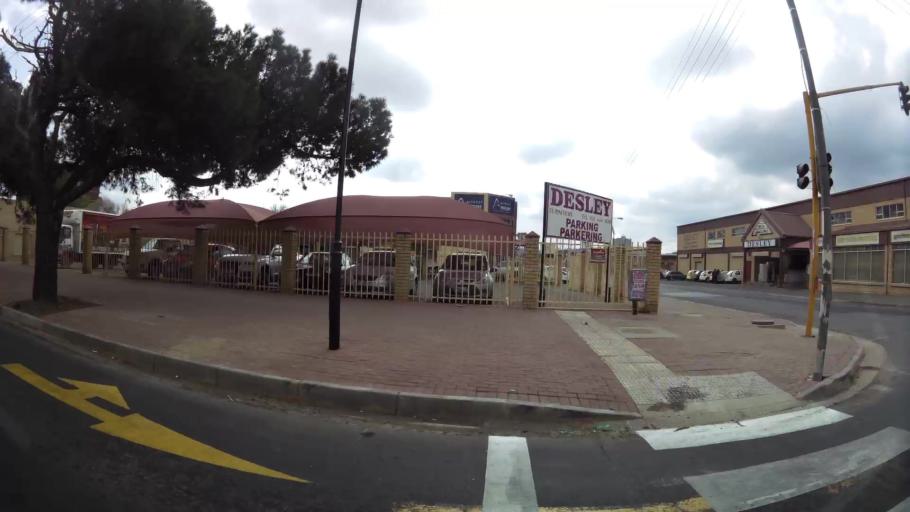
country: ZA
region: Orange Free State
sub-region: Mangaung Metropolitan Municipality
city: Bloemfontein
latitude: -29.1222
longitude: 26.2034
